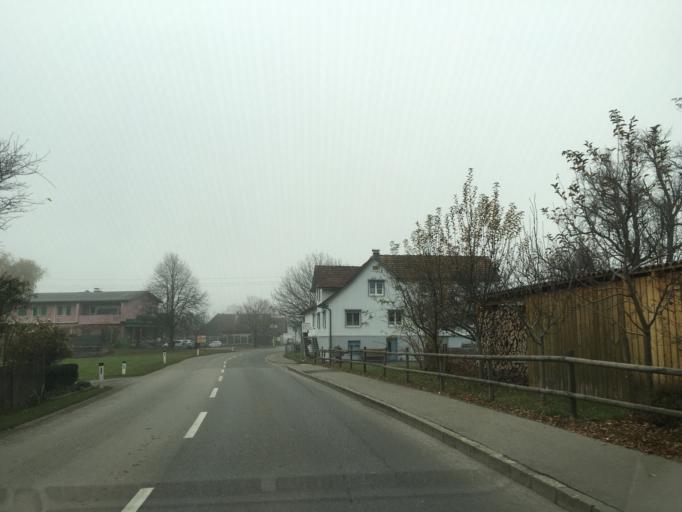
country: AT
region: Vorarlberg
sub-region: Politischer Bezirk Feldkirch
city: Koblach
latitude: 47.3170
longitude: 9.6012
